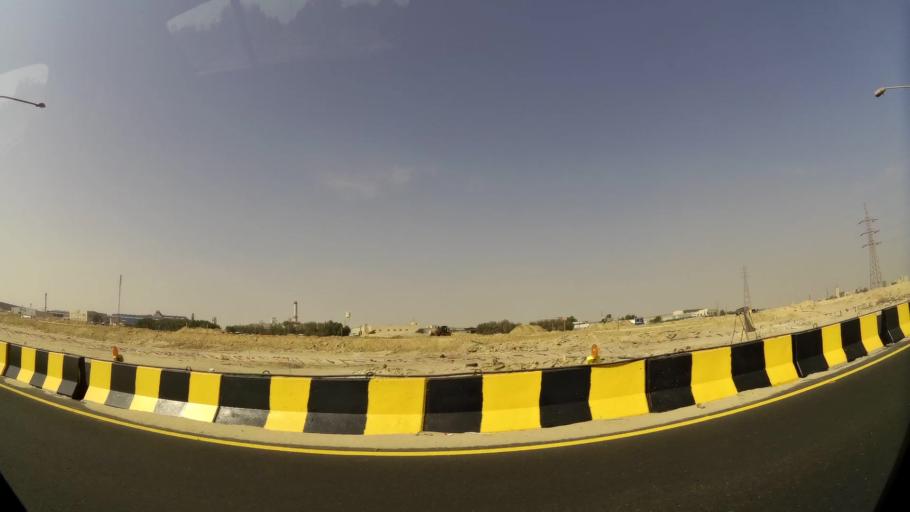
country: KW
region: Al Ahmadi
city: Al Fahahil
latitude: 28.9920
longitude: 48.1403
